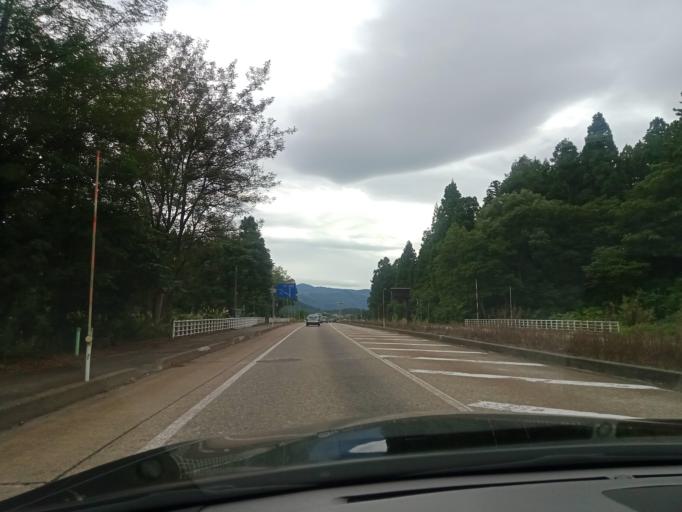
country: JP
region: Niigata
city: Arai
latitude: 36.9711
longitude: 138.2244
